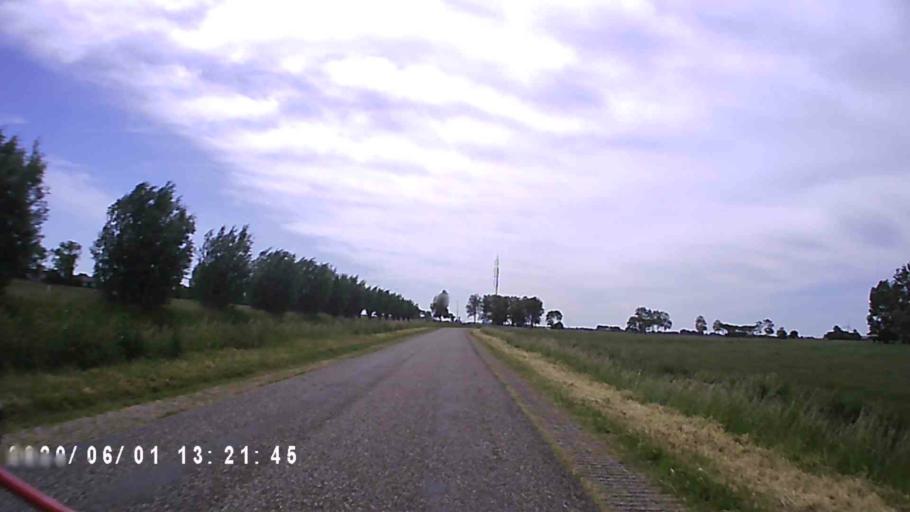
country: NL
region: Friesland
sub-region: Gemeente Littenseradiel
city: Wommels
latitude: 53.1106
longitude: 5.5827
